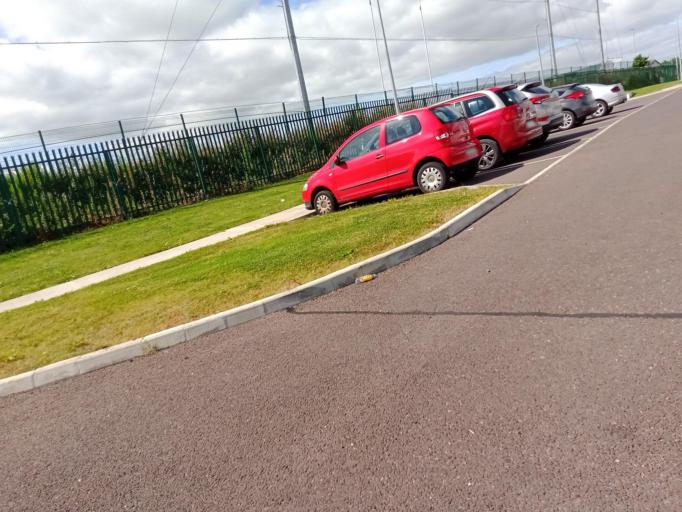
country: IE
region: Leinster
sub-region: Kilkenny
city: Callan
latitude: 52.5397
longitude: -7.3858
